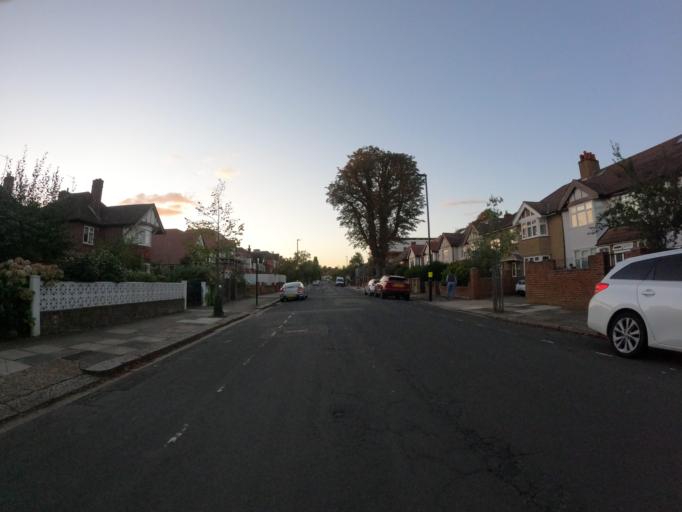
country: GB
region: England
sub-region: Greater London
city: Acton
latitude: 51.5134
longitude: -0.2749
